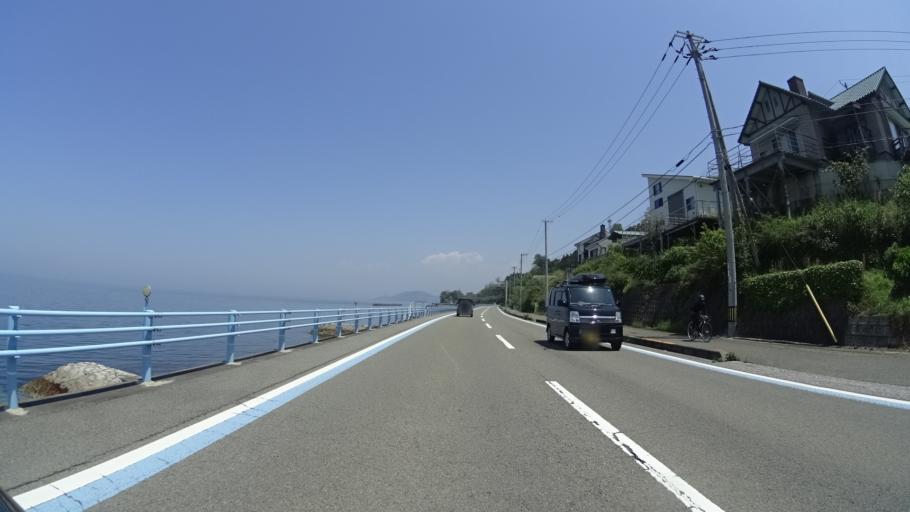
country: JP
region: Ehime
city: Iyo
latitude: 33.6731
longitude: 132.6127
